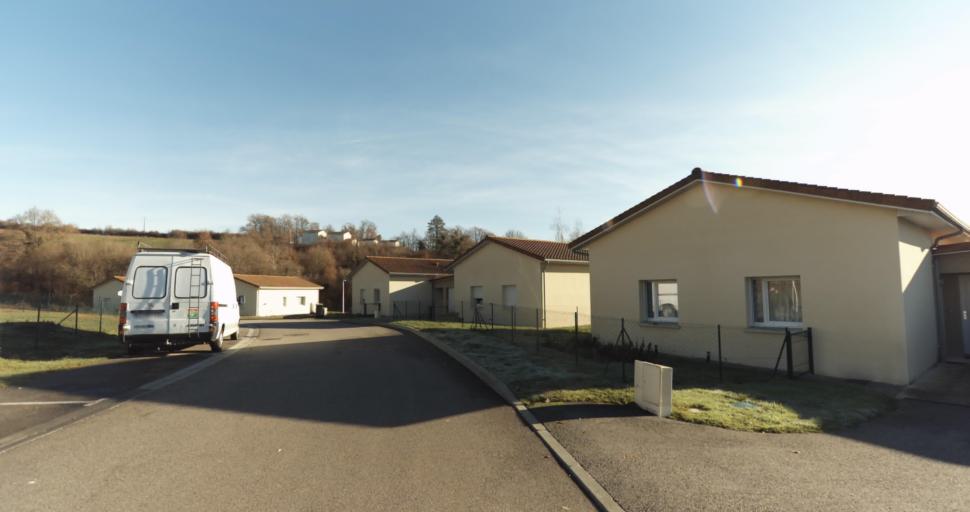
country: FR
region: Limousin
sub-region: Departement de la Haute-Vienne
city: Aixe-sur-Vienne
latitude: 45.8071
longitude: 1.1504
